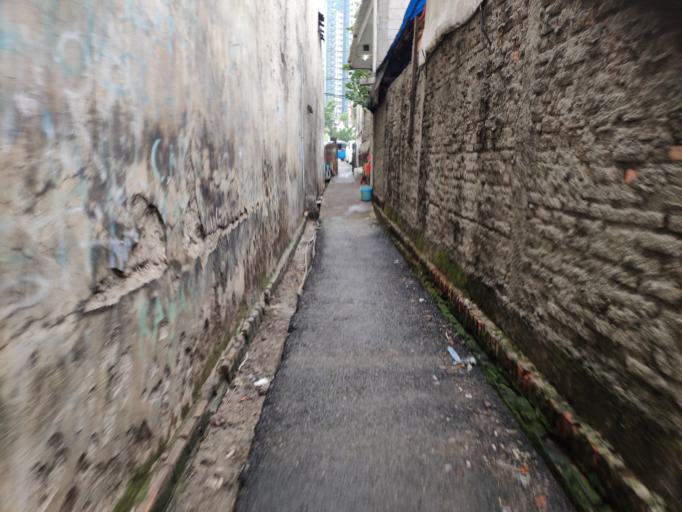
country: ID
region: Jakarta Raya
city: Jakarta
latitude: -6.1976
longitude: 106.8573
